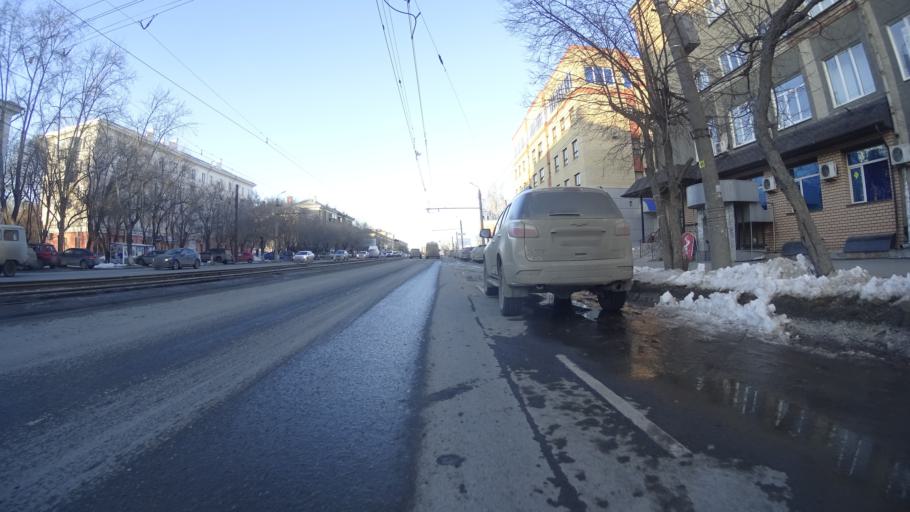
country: RU
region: Chelyabinsk
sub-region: Gorod Chelyabinsk
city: Chelyabinsk
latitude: 55.1422
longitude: 61.4429
